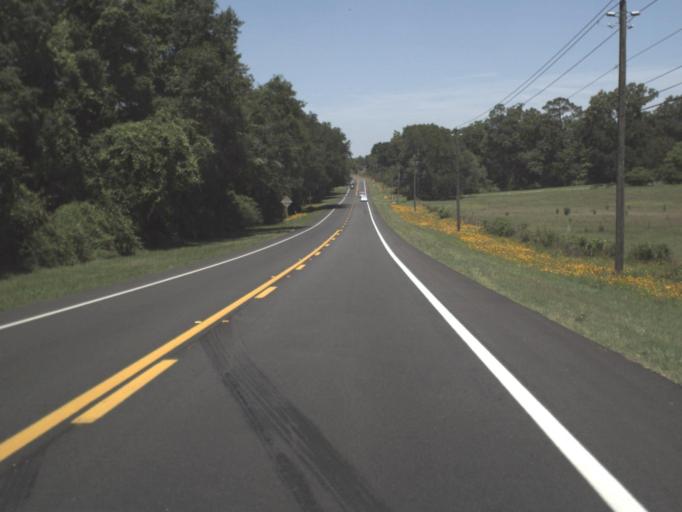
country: US
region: Florida
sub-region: Suwannee County
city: Wellborn
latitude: 30.1968
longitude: -82.7605
